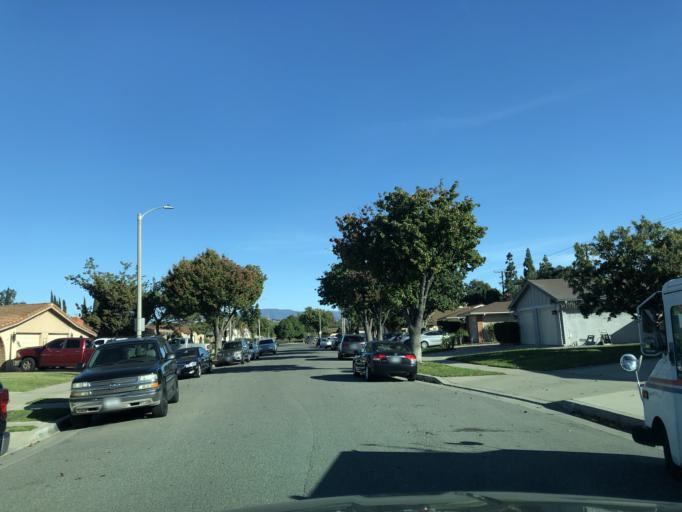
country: US
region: California
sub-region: Orange County
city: Orange
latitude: 33.7737
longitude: -117.8337
